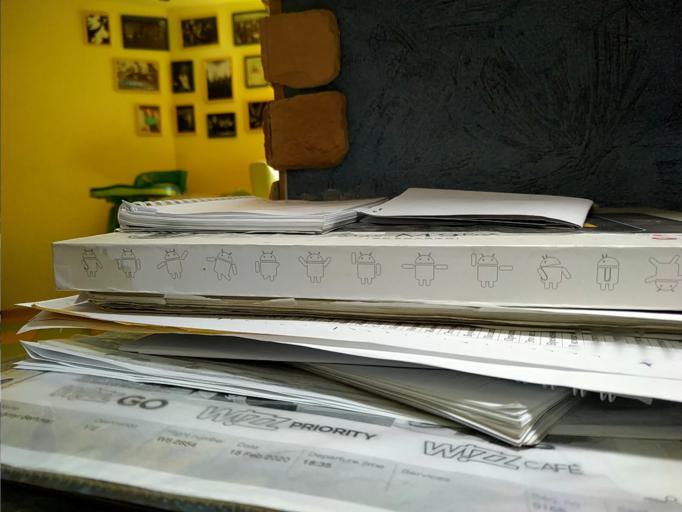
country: RU
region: Novgorod
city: Sol'tsy
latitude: 58.0570
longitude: 30.1706
